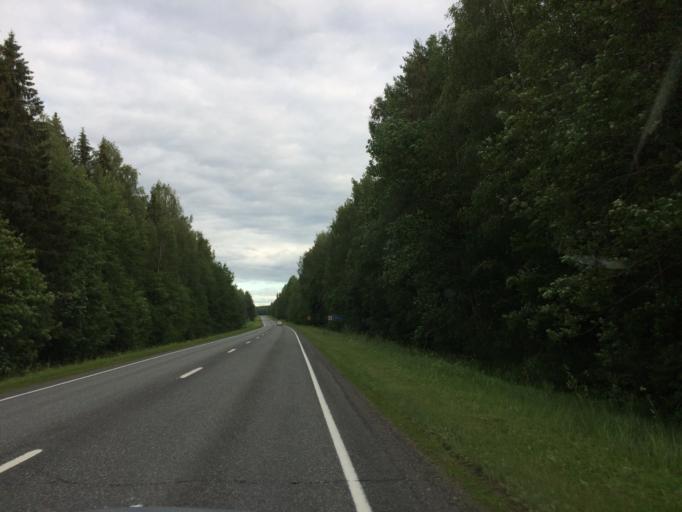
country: FI
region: Haeme
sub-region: Haemeenlinna
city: Haemeenlinna
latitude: 60.9380
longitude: 24.5223
